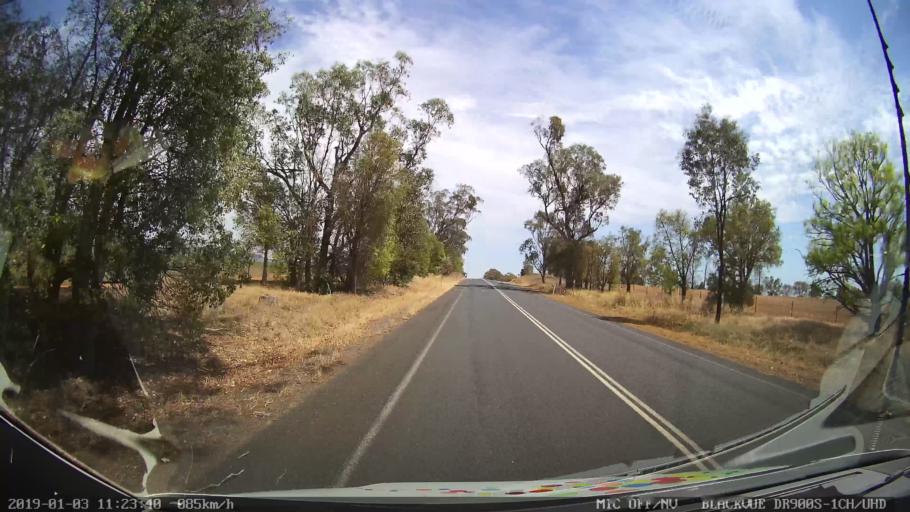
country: AU
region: New South Wales
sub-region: Weddin
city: Grenfell
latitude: -34.0606
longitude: 148.2410
